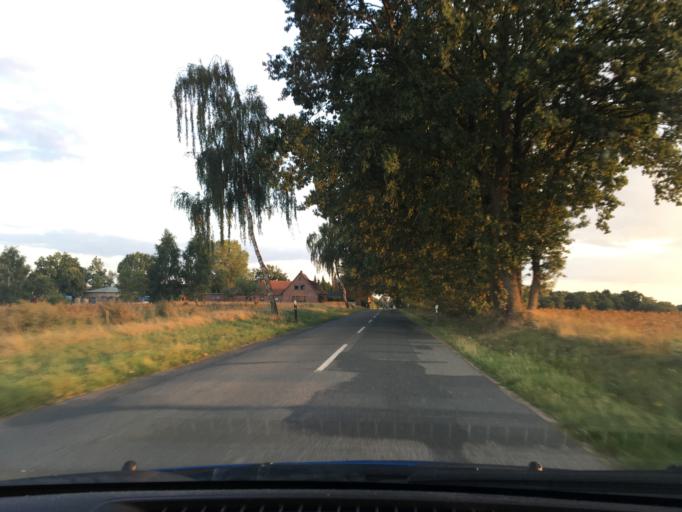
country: DE
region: Lower Saxony
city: Nahrendorf
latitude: 53.1815
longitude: 10.8160
